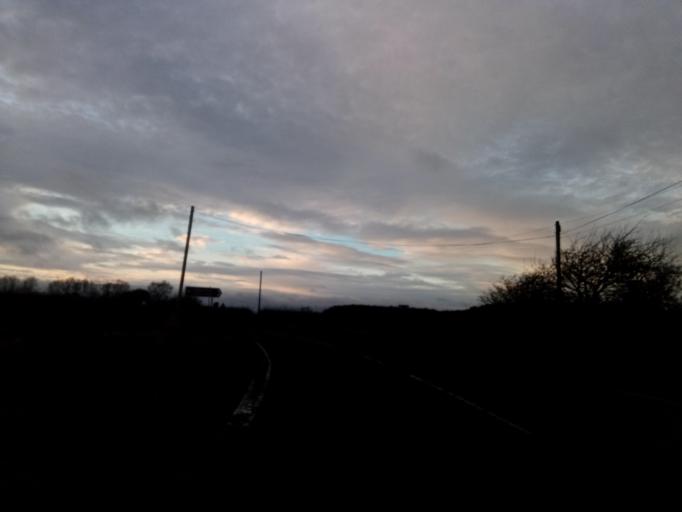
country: GB
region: England
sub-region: Newcastle upon Tyne
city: Dinnington
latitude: 55.0739
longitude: -1.6942
